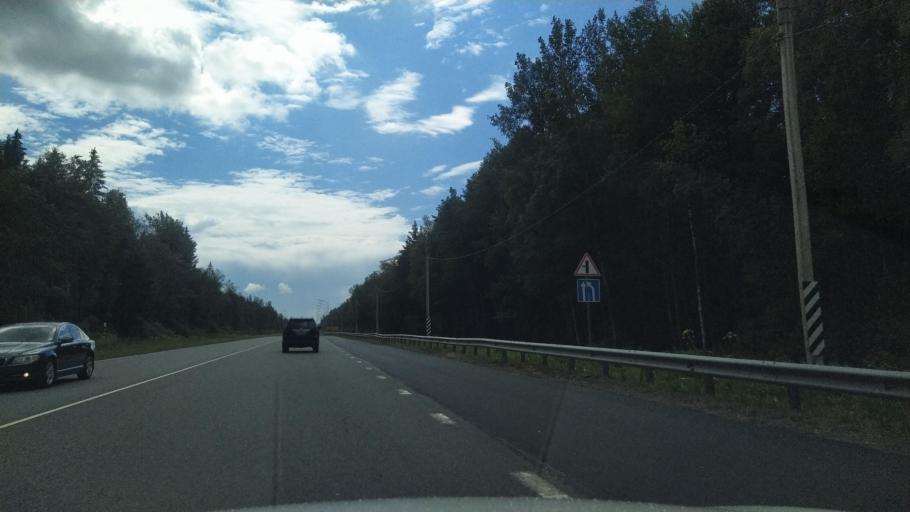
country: RU
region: Leningrad
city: Rozhdestveno
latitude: 59.3863
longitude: 29.9693
